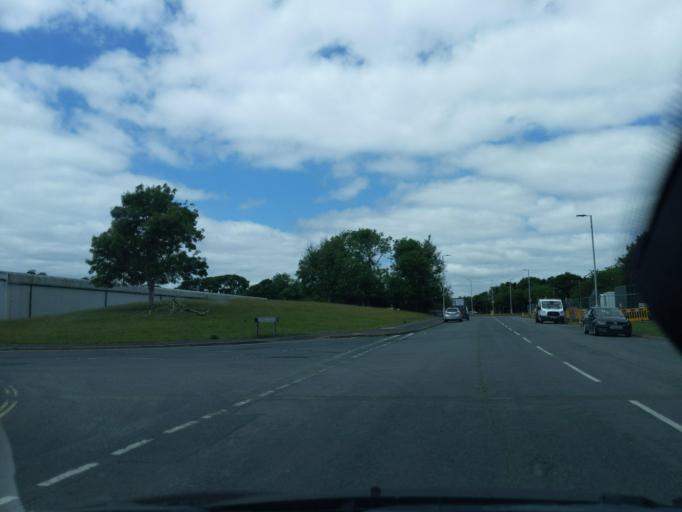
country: GB
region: England
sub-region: Devon
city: Plympton
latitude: 50.4153
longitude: -4.0880
